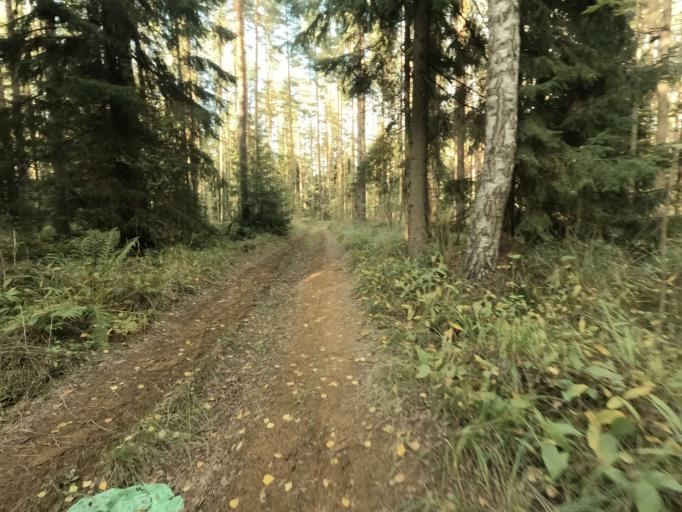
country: RU
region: Leningrad
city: Imeni Sverdlova
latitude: 59.8453
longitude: 30.7298
